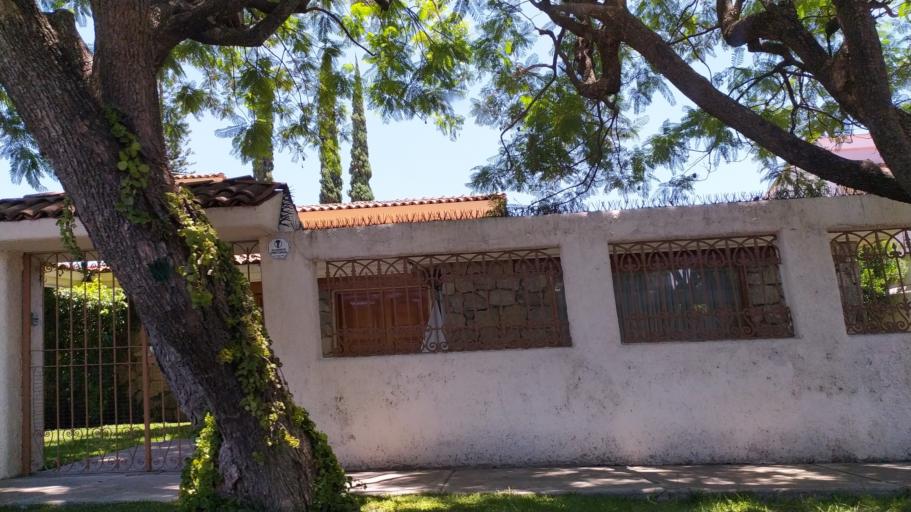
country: MX
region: Jalisco
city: Guadalajara
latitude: 20.6880
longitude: -103.4064
